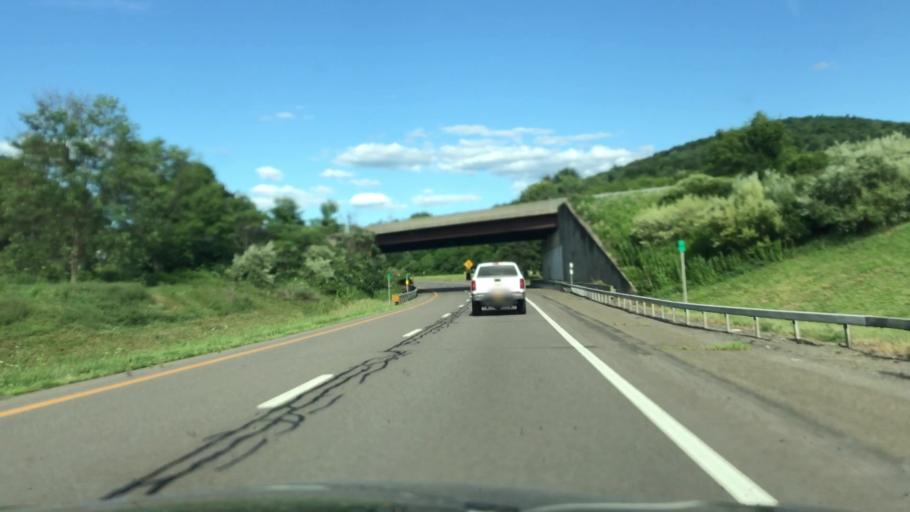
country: US
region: New York
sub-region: Broome County
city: Chenango Bridge
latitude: 42.0996
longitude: -75.8155
